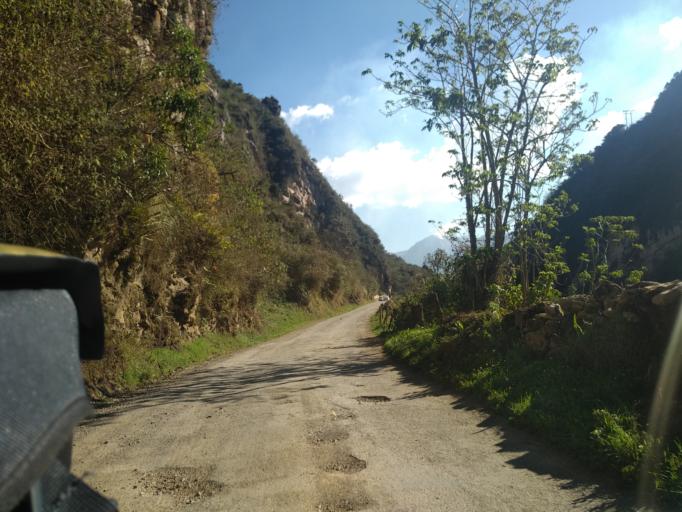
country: PE
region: Amazonas
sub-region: Provincia de Chachapoyas
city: Montevideo
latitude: -6.7240
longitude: -77.8251
